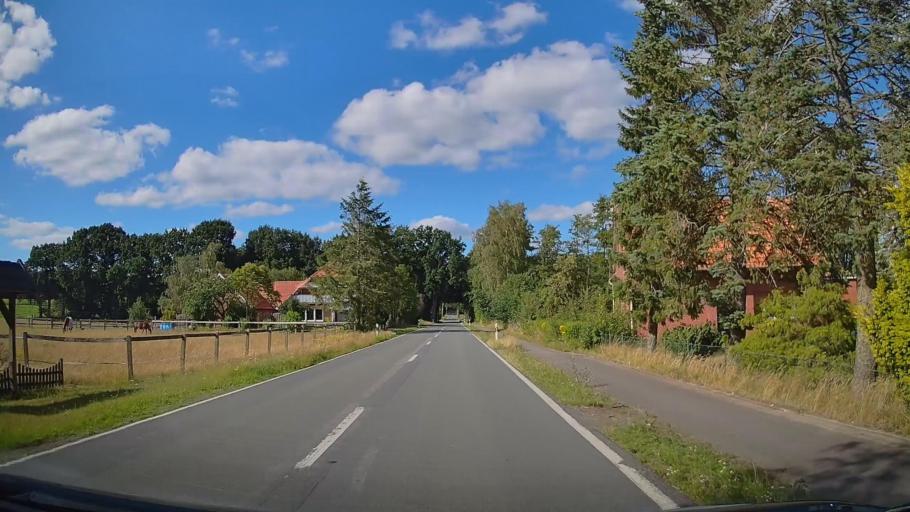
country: DE
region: Lower Saxony
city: Bippen
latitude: 52.5876
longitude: 7.7407
